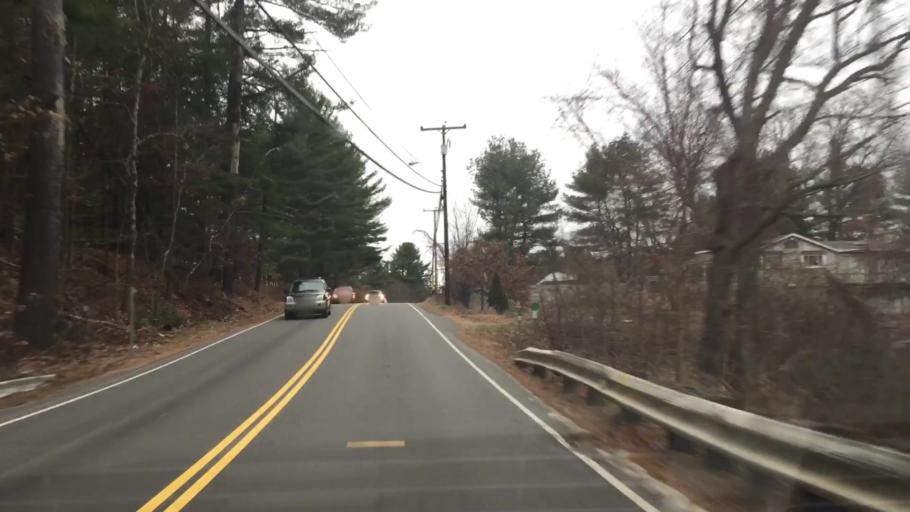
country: US
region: Massachusetts
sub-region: Middlesex County
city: Tyngsboro
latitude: 42.7116
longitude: -71.4074
